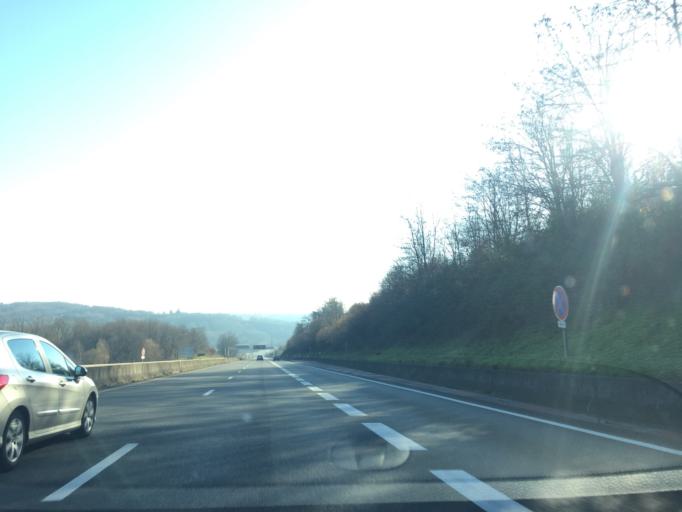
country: FR
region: Limousin
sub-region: Departement de la Correze
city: Donzenac
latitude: 45.2211
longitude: 1.5118
